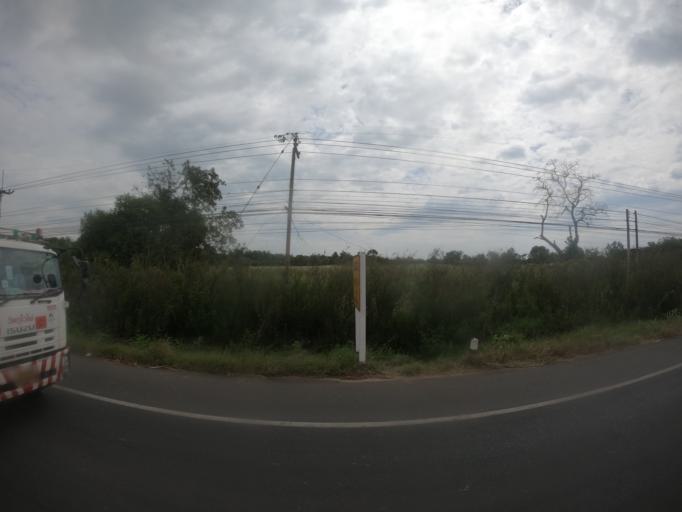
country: TH
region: Maha Sarakham
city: Kantharawichai
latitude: 16.2576
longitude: 103.2798
